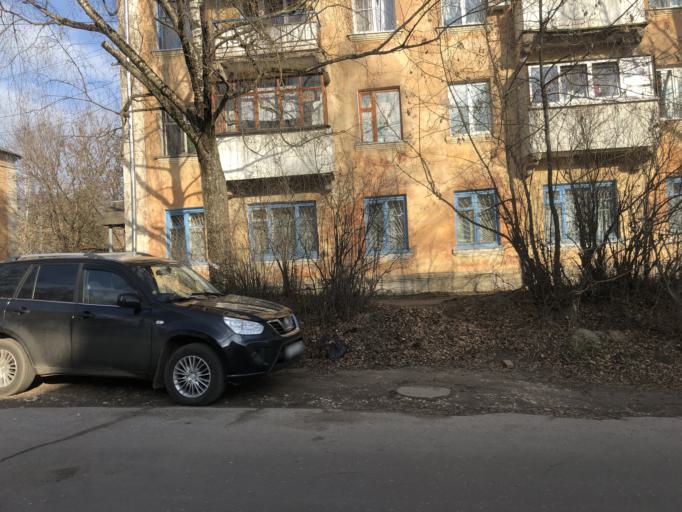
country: RU
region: Tverskaya
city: Rzhev
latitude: 56.2625
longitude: 34.3393
